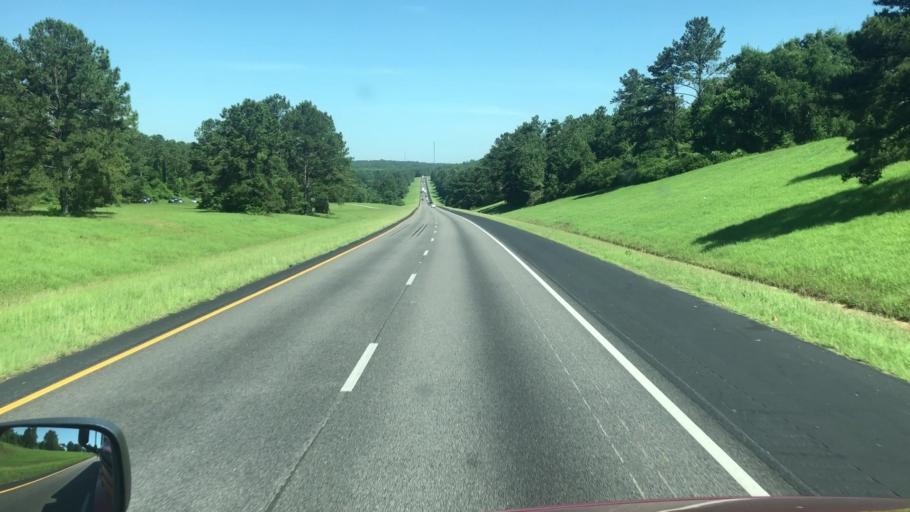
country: US
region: Alabama
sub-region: Autauga County
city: Prattville
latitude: 32.5106
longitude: -86.4249
